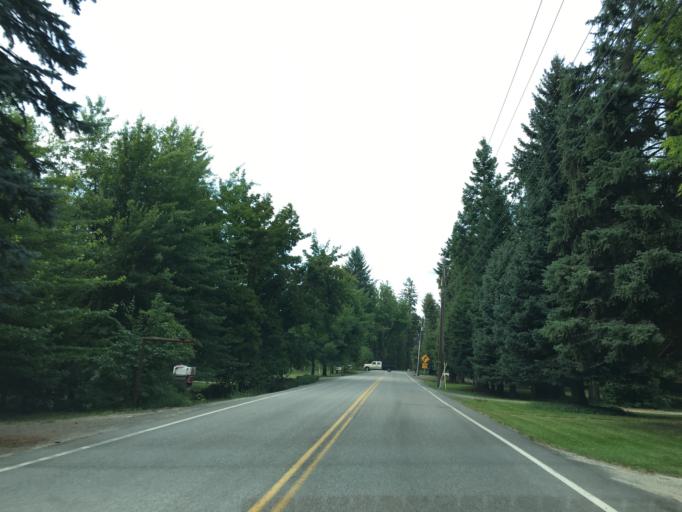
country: US
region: Washington
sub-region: Chelan County
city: Leavenworth
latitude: 47.5891
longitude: -120.6596
